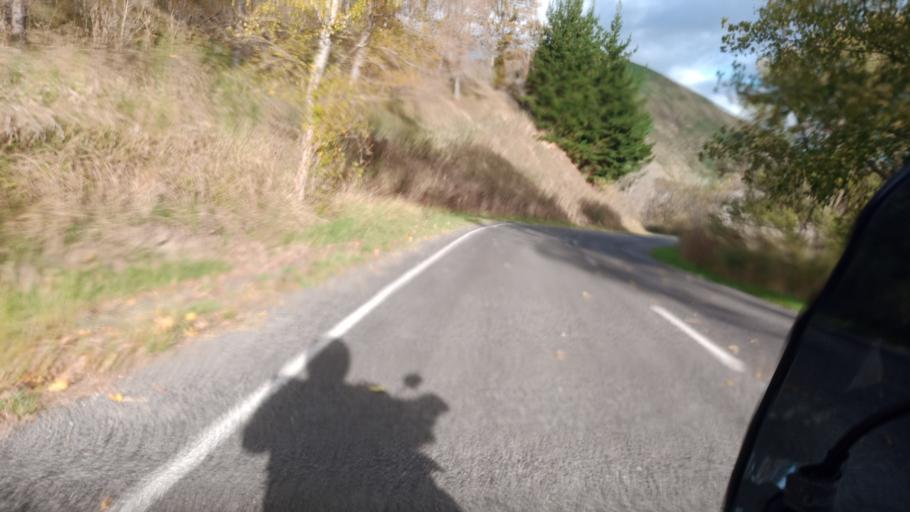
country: NZ
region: Gisborne
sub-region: Gisborne District
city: Gisborne
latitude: -38.5500
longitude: 177.6907
